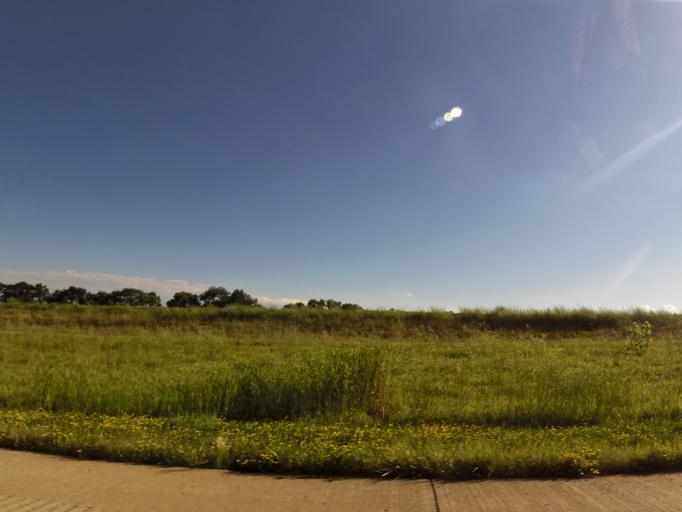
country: US
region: Missouri
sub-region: Ralls County
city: New London
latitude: 39.5448
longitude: -91.3747
